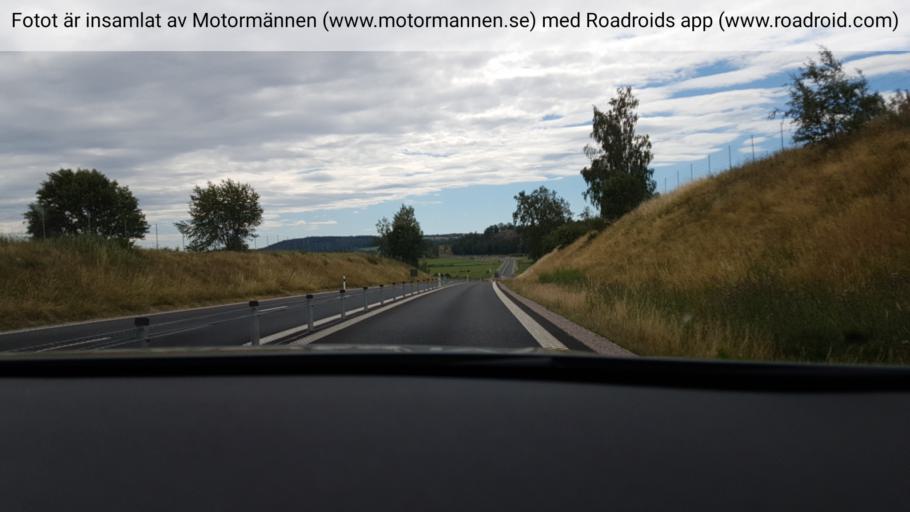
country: SE
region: Joenkoeping
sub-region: Tranas Kommun
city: Tranas
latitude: 58.0104
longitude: 14.9319
